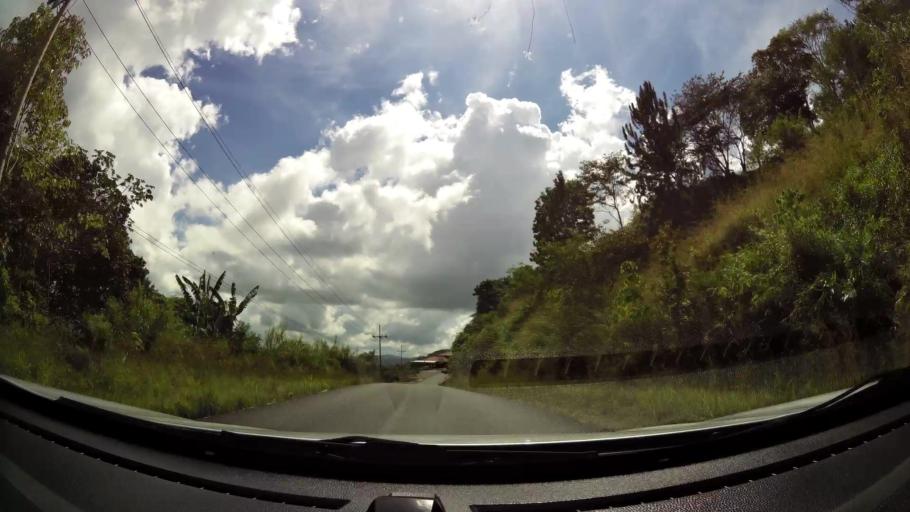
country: CR
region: San Jose
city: San Isidro
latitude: 9.3343
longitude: -83.7339
